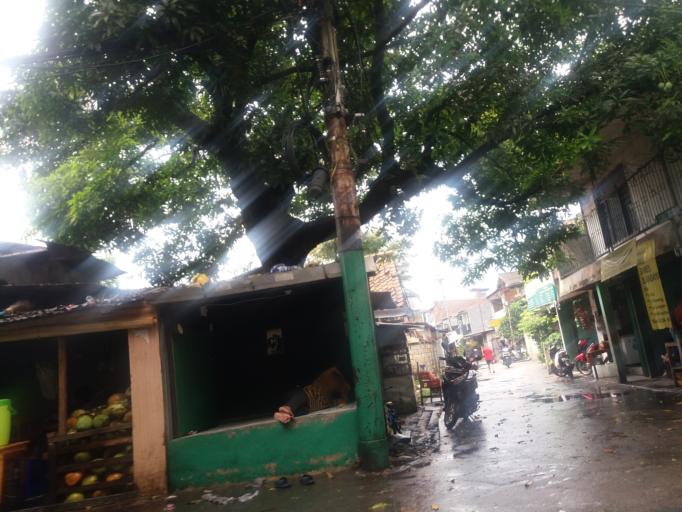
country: ID
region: Jakarta Raya
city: Jakarta
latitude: -6.2126
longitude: 106.8245
